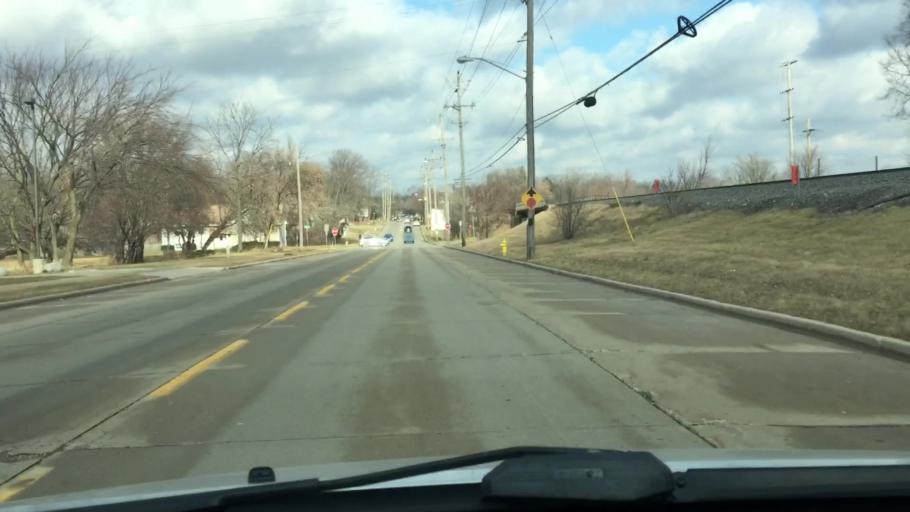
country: US
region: Wisconsin
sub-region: Waukesha County
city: Waukesha
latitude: 42.9985
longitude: -88.2369
